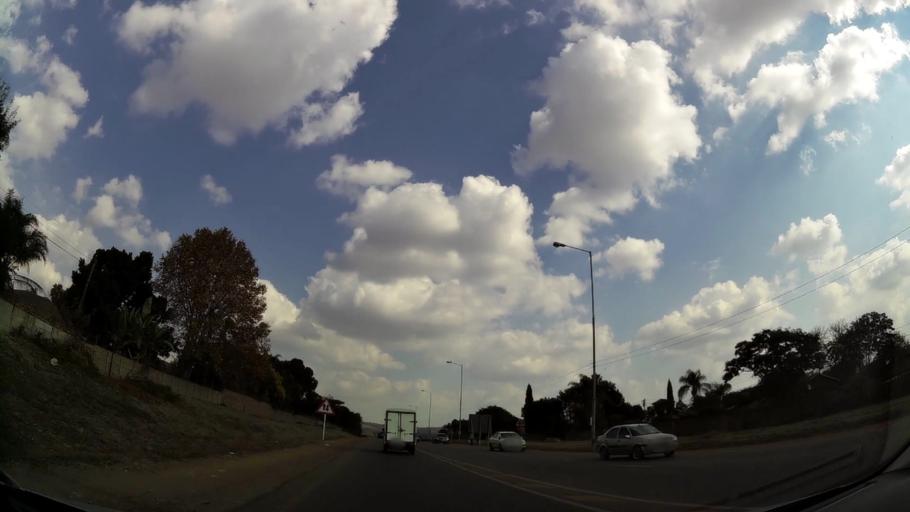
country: ZA
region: Gauteng
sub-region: City of Tshwane Metropolitan Municipality
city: Pretoria
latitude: -25.7996
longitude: 28.3147
